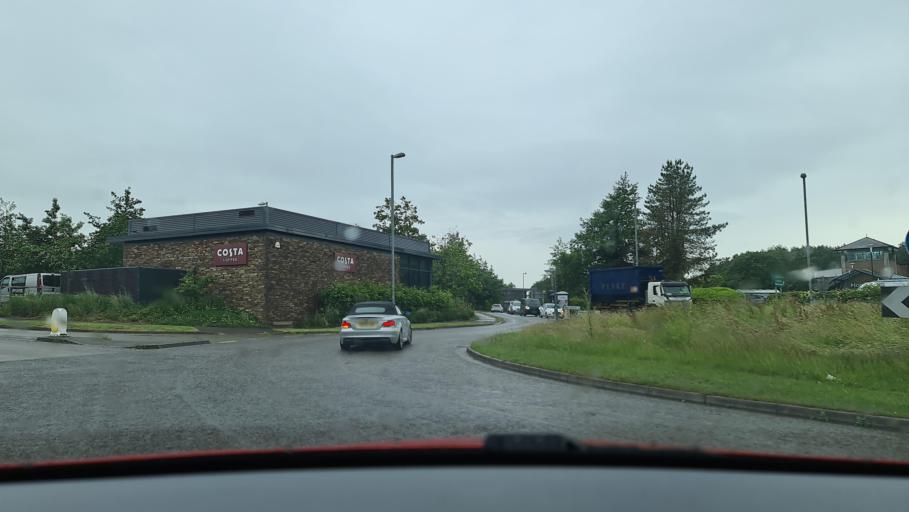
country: GB
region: England
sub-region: Cornwall
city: Liskeard
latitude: 50.4506
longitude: -4.4505
